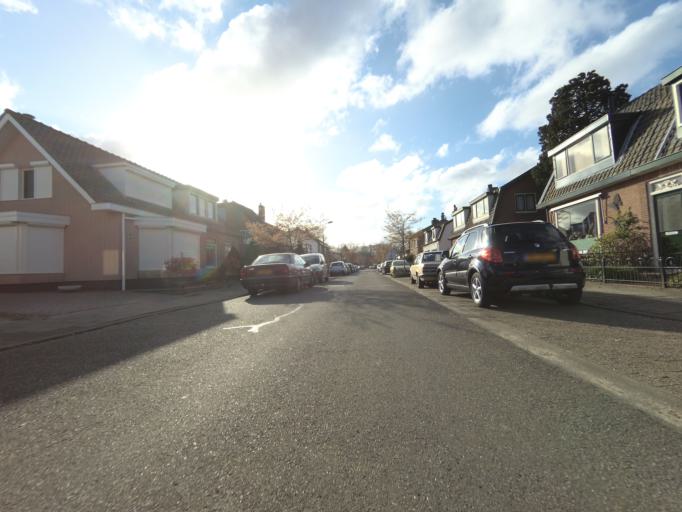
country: NL
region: Utrecht
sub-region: Gemeente Utrechtse Heuvelrug
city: Driebergen-Rijsenburg
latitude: 52.0553
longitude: 5.2929
